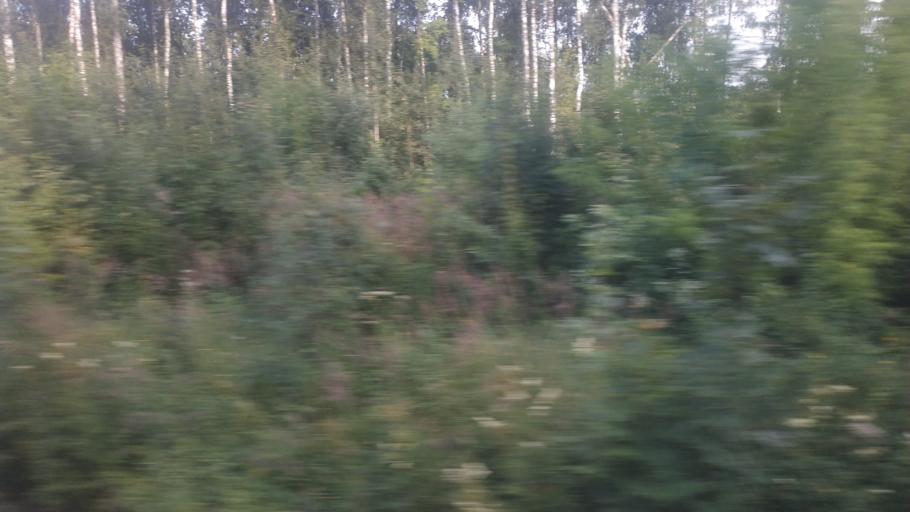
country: RU
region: Moskovskaya
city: Tugolesskiy Bor
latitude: 55.5519
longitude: 39.6938
